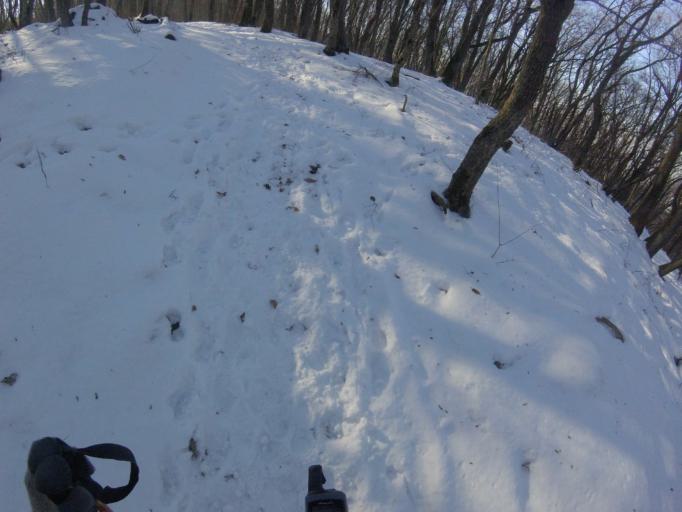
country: SK
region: Nitriansky
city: Sahy
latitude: 47.9837
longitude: 18.8884
